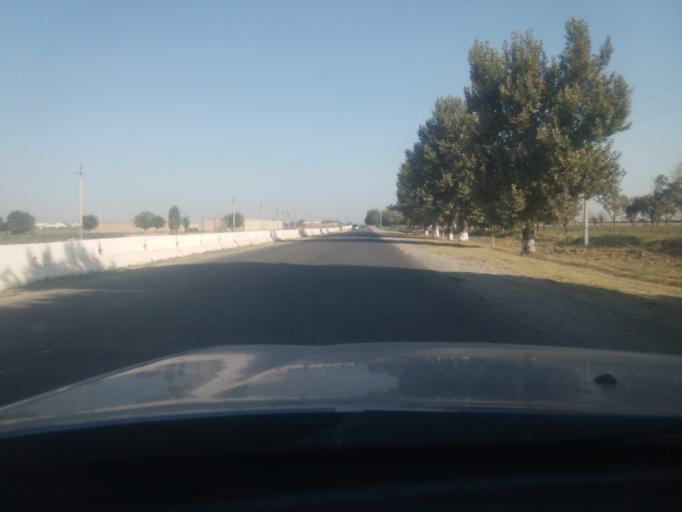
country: UZ
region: Sirdaryo
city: Guliston
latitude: 40.5037
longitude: 68.7975
